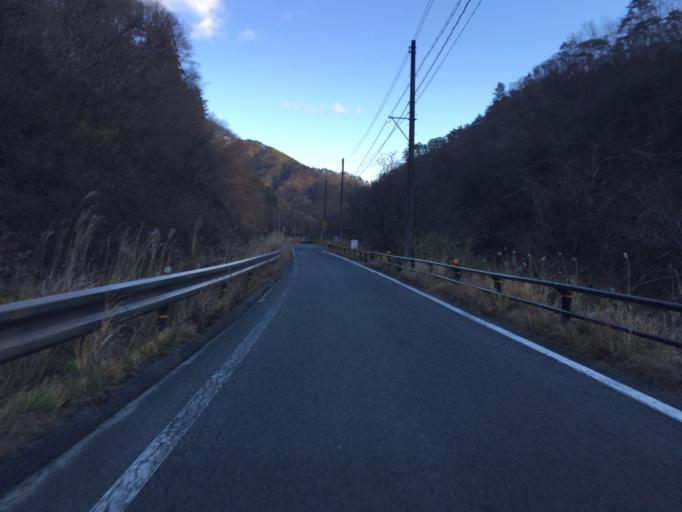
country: JP
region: Fukushima
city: Iwaki
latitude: 37.1998
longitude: 140.7755
